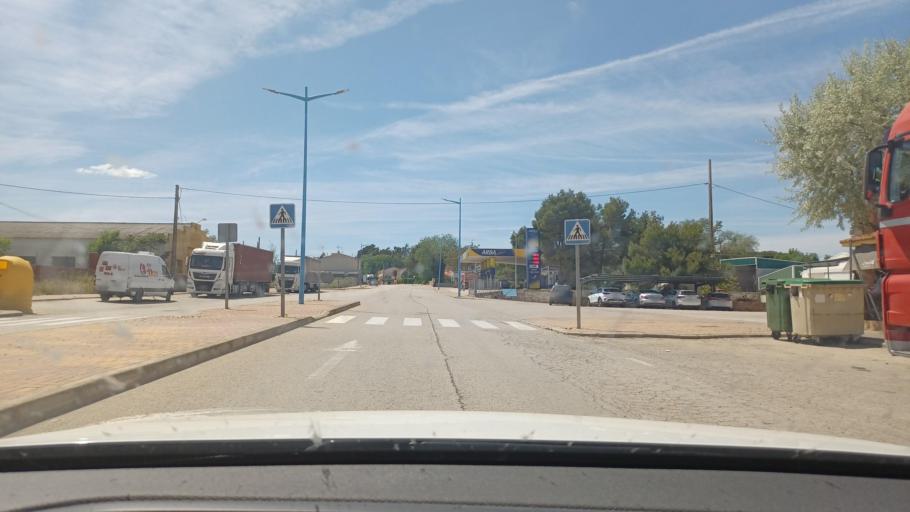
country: ES
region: Castille-La Mancha
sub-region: Provincia de Cuenca
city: Montalbo
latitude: 39.8816
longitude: -2.6671
